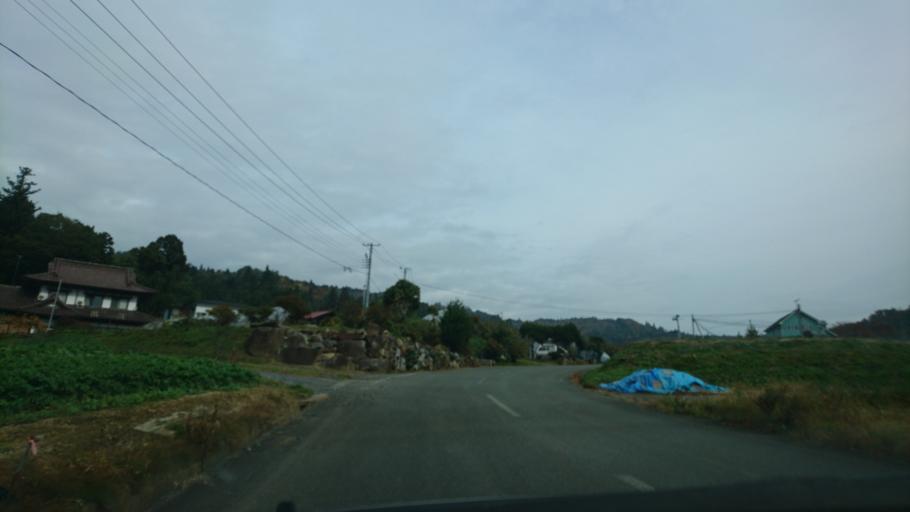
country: JP
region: Iwate
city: Ichinoseki
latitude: 38.9745
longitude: 141.1799
